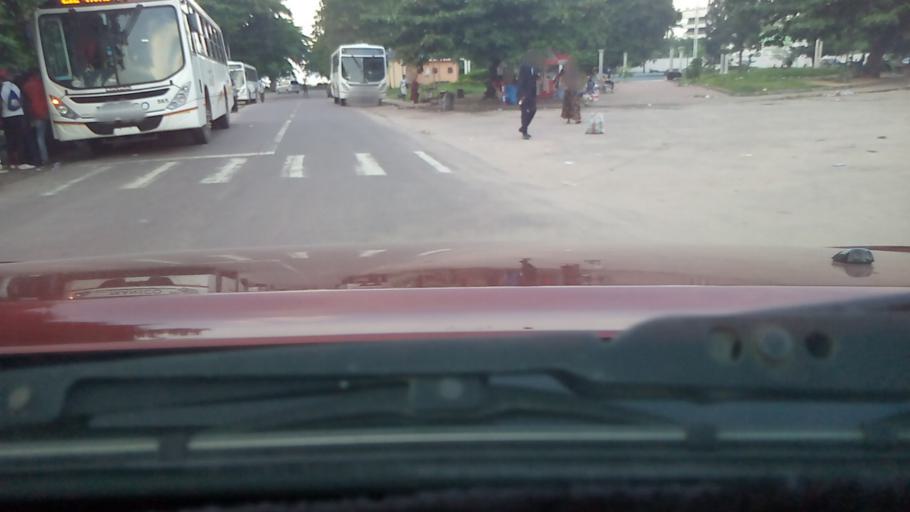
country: CD
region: Kinshasa
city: Kinshasa
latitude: -4.3061
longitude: 15.2870
